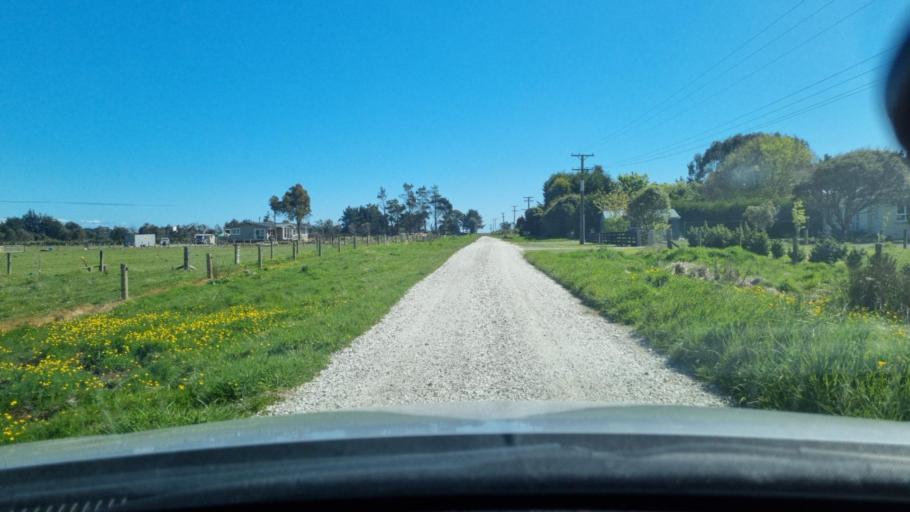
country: NZ
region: Southland
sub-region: Invercargill City
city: Invercargill
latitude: -46.3909
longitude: 168.2979
